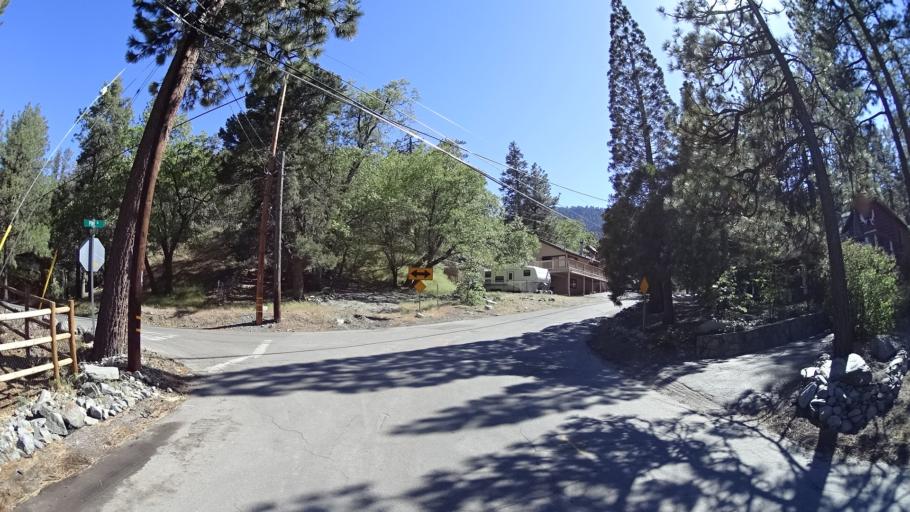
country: US
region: California
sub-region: San Bernardino County
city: Wrightwood
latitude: 34.3554
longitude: -117.6377
